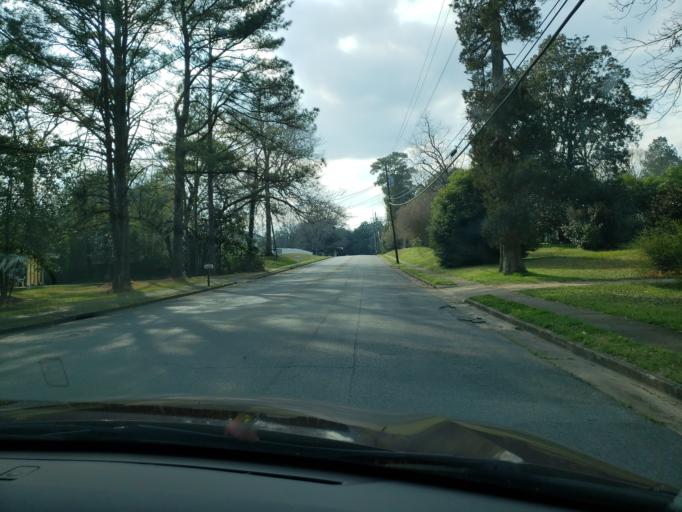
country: US
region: Alabama
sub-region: Hale County
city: Greensboro
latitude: 32.7042
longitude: -87.6038
